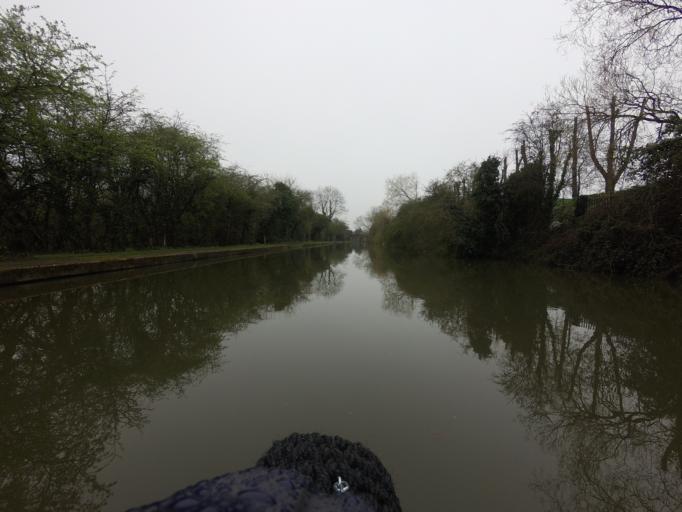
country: GB
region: England
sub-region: Milton Keynes
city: Simpson
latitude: 52.0110
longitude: -0.7160
